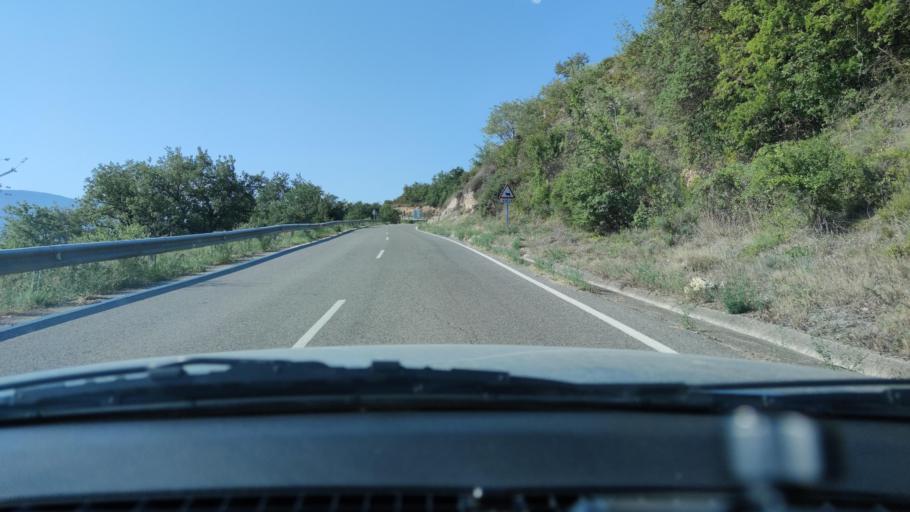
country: ES
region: Catalonia
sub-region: Provincia de Lleida
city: Llimiana
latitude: 42.0924
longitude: 0.8749
